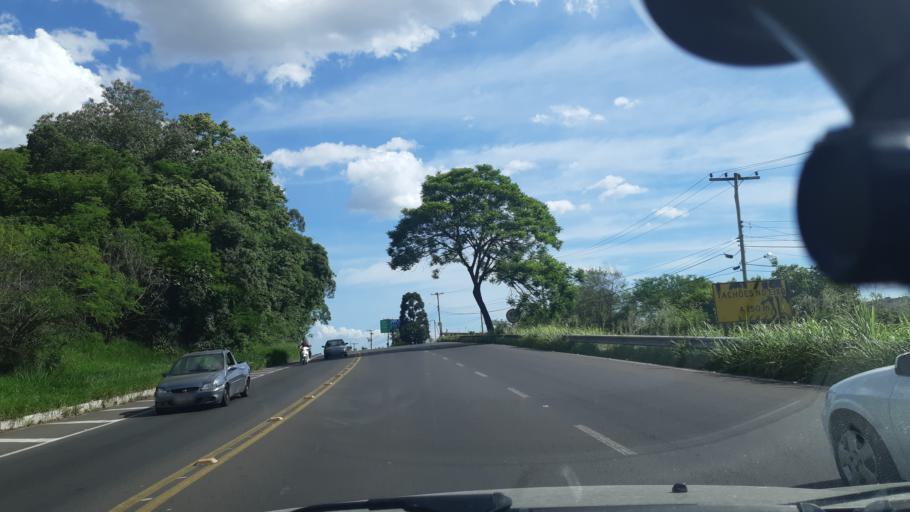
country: BR
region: Rio Grande do Sul
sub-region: Estancia Velha
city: Estancia Velha
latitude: -29.6517
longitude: -51.1446
